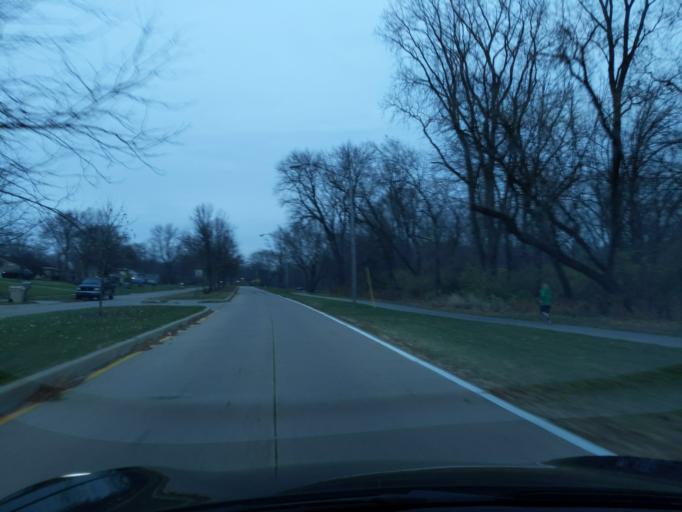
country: US
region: Indiana
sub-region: Saint Joseph County
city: Notre Dame
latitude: 41.7259
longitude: -86.2696
